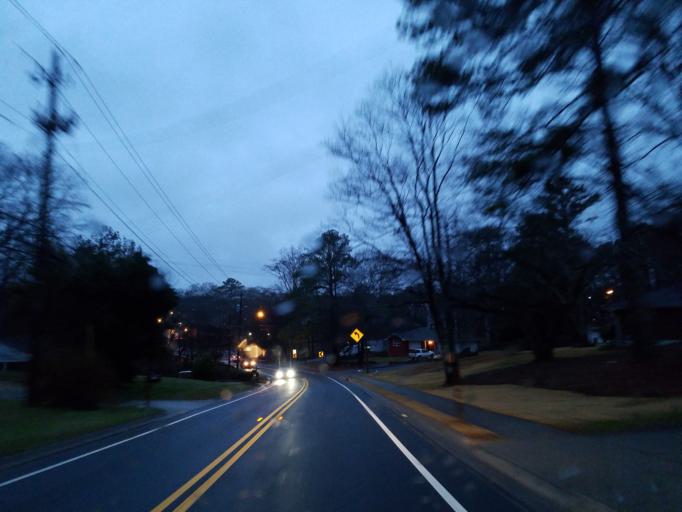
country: US
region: Georgia
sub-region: Fulton County
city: Roswell
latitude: 34.0264
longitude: -84.3506
